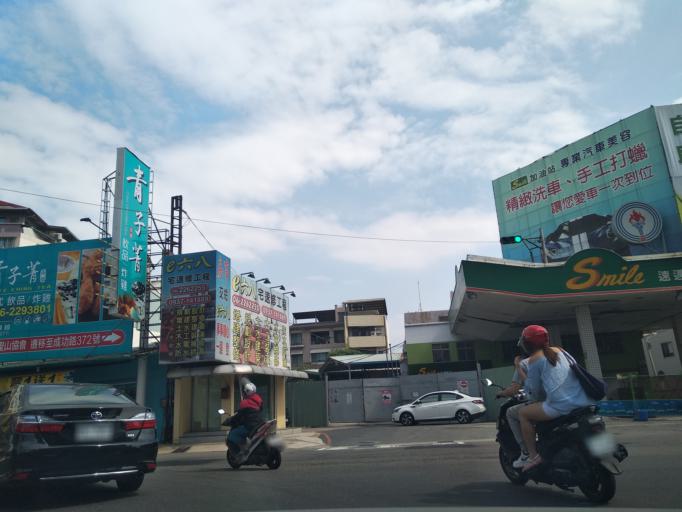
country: TW
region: Taiwan
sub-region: Tainan
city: Tainan
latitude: 23.0039
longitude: 120.2042
